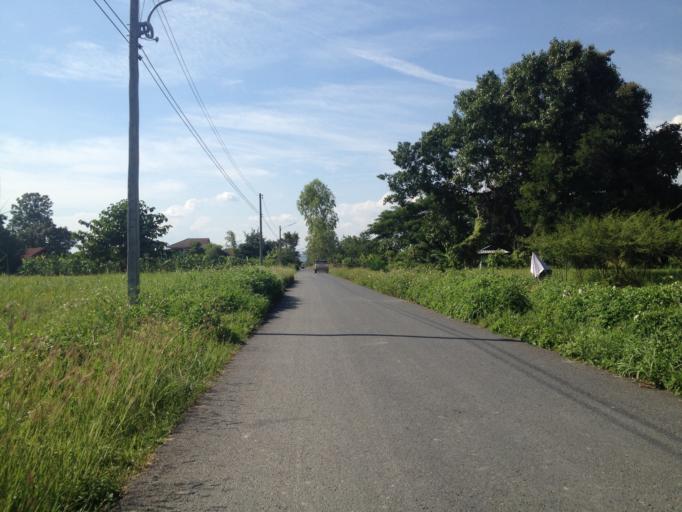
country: TH
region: Chiang Mai
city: Hang Dong
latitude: 18.7218
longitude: 98.9682
